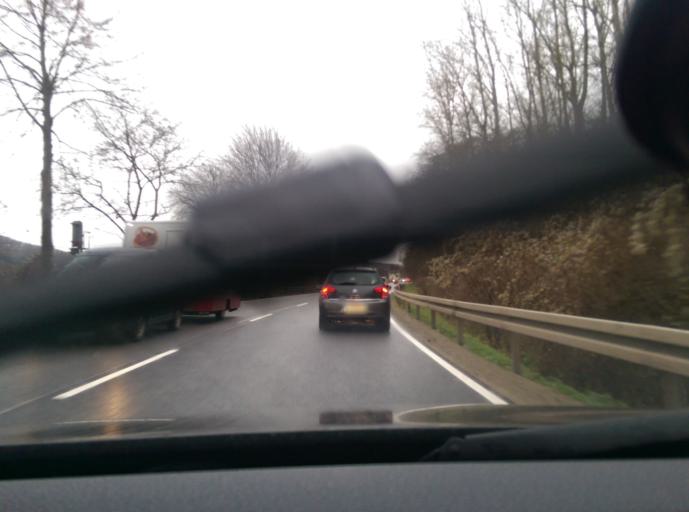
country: DE
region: Hesse
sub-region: Regierungsbezirk Kassel
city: Sontra
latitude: 51.1185
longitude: 9.9751
